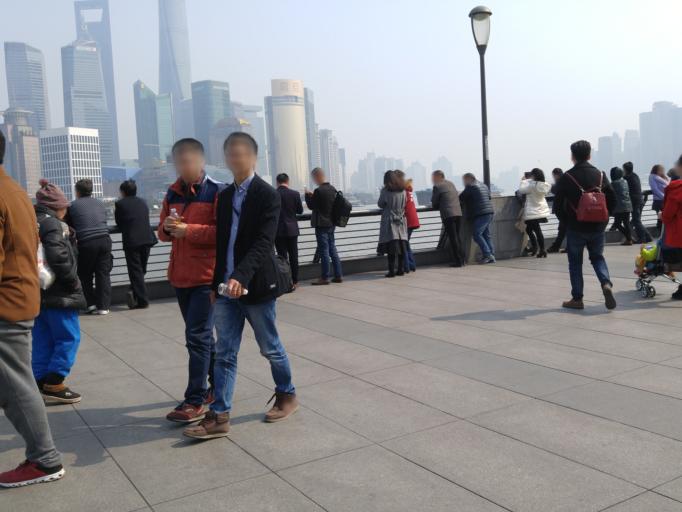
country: CN
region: Shanghai Shi
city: Hongkou
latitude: 31.2415
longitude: 121.4862
